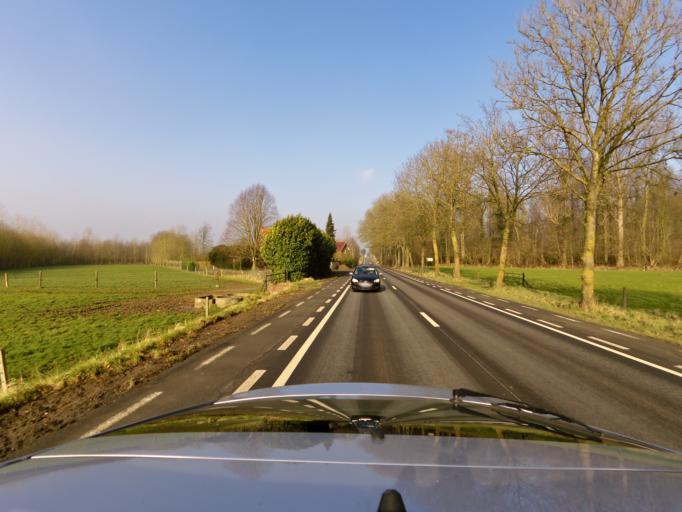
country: BE
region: Wallonia
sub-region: Province du Hainaut
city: Peruwelz
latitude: 50.5647
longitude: 3.5763
